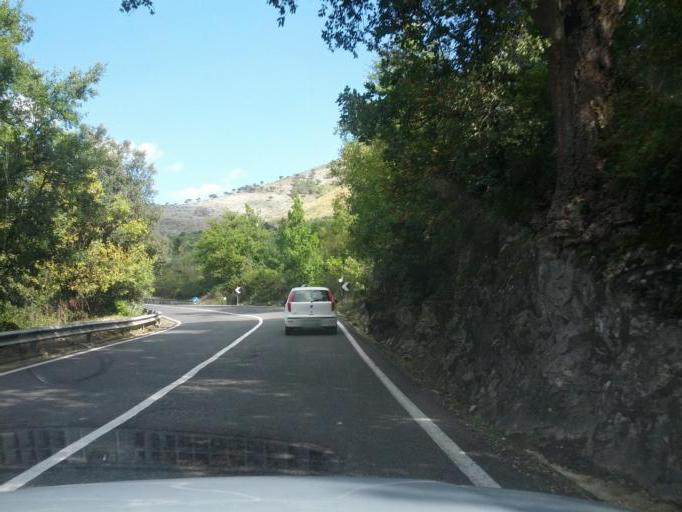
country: IT
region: Latium
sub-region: Provincia di Latina
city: Itri
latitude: 41.3039
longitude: 13.4959
